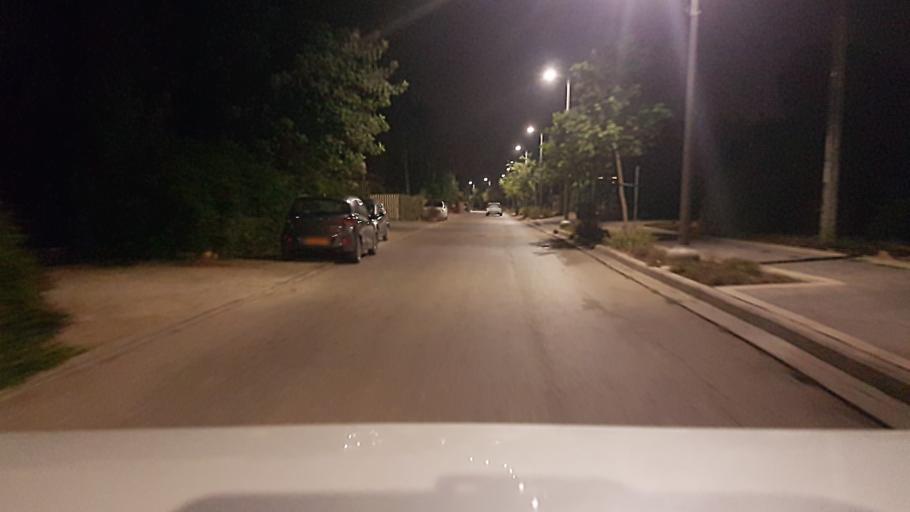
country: IL
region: Central District
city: Nehalim
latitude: 32.0770
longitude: 34.9299
